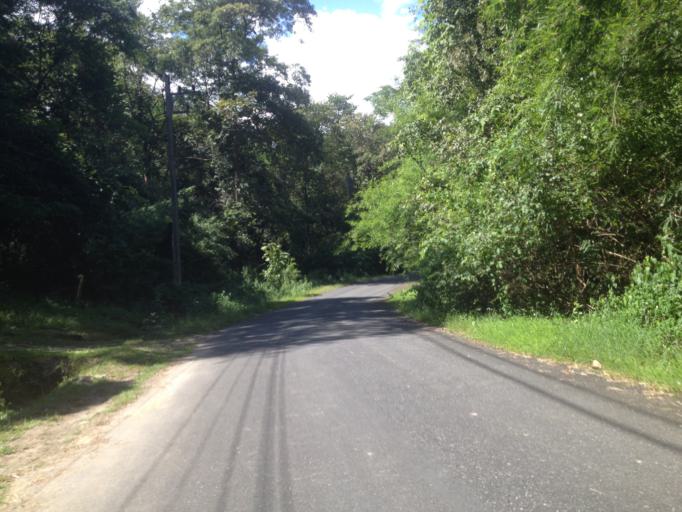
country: TH
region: Chiang Mai
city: Chiang Mai
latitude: 18.7914
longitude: 98.9443
